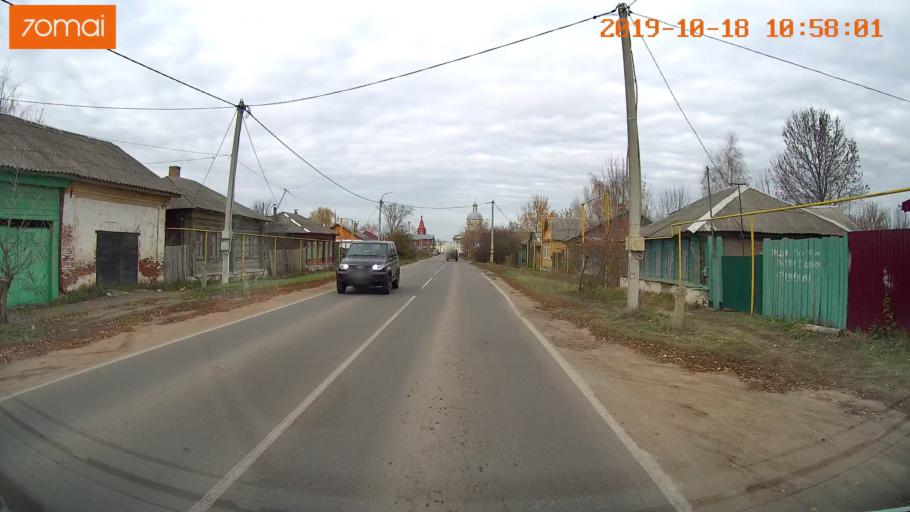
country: RU
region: Tula
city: Yepifan'
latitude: 53.8236
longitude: 38.5569
